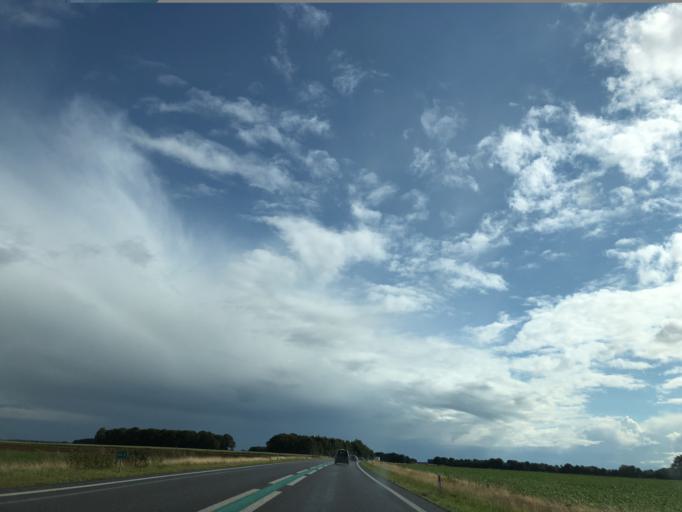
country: NL
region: Drenthe
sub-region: Gemeente Borger-Odoorn
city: Borger
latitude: 52.9497
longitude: 6.7837
